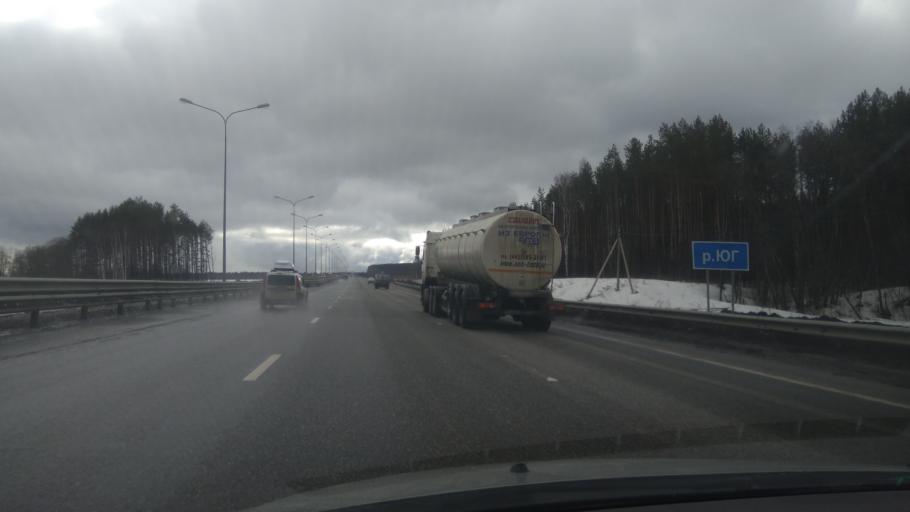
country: RU
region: Perm
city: Bershet'
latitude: 57.7197
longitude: 56.3573
